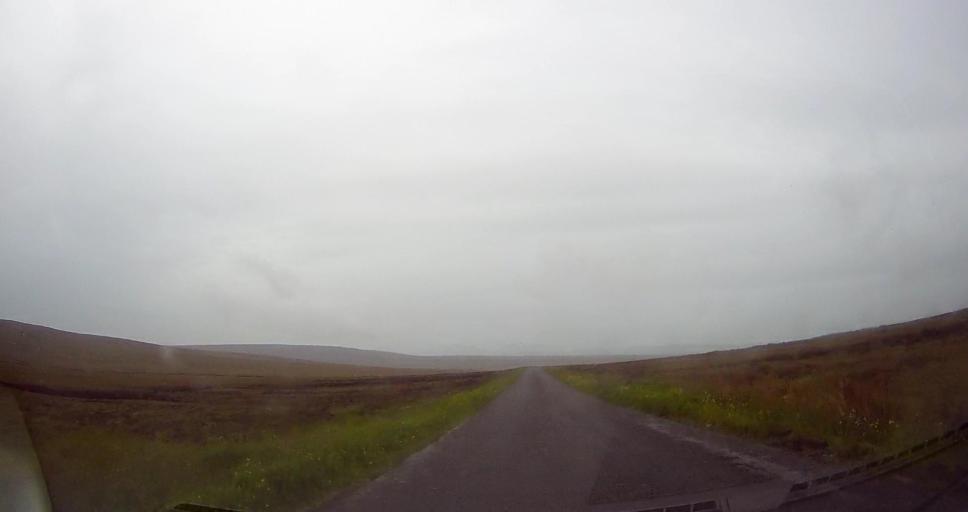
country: GB
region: Scotland
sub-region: Orkney Islands
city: Stromness
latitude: 59.0994
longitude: -3.1497
